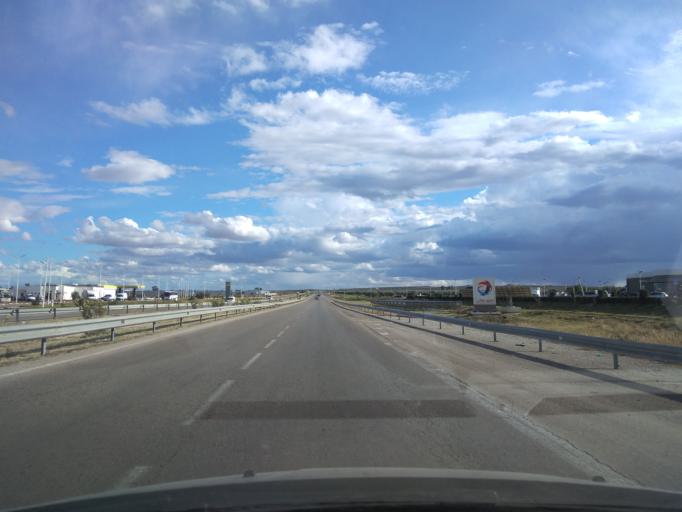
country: TN
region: Al Munastir
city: Manzil Kamil
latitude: 35.5689
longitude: 10.6131
